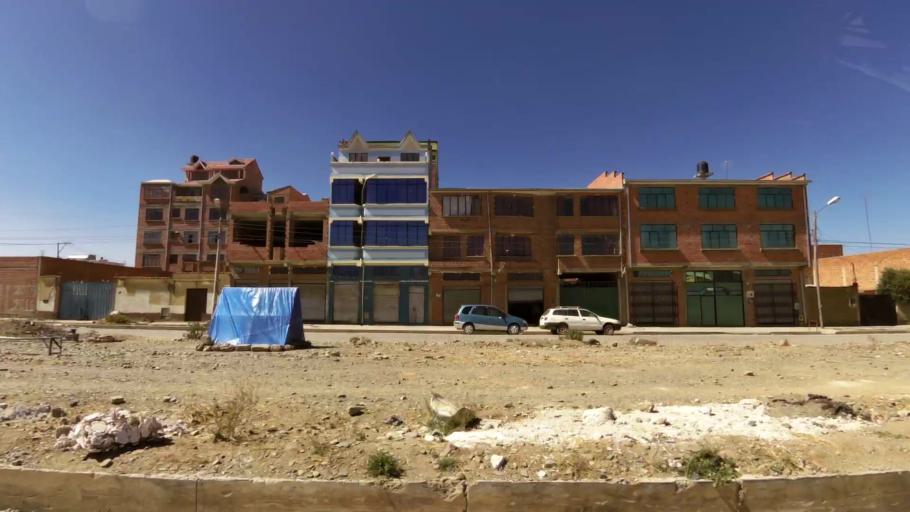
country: BO
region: La Paz
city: La Paz
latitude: -16.5360
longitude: -68.1933
